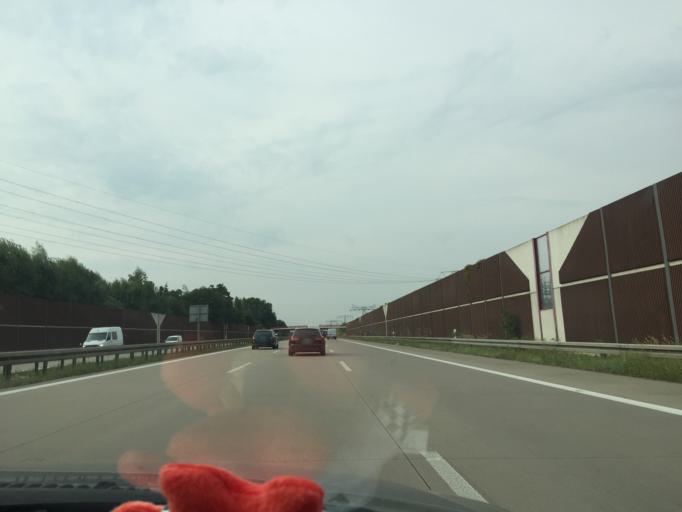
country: DE
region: Brandenburg
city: Neuenhagen
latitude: 52.5129
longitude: 13.7305
